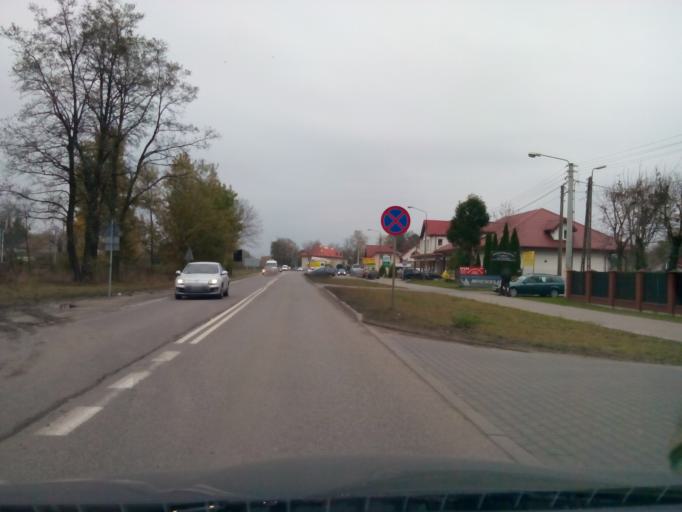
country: PL
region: Masovian Voivodeship
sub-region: Powiat zyrardowski
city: Radziejowice
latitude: 52.0846
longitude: 20.5466
